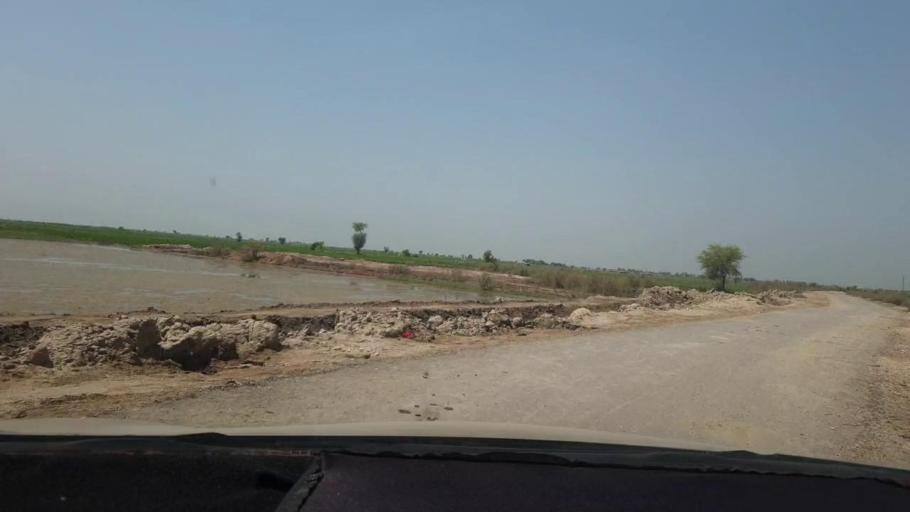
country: PK
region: Sindh
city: Shahdadkot
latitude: 27.8333
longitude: 67.8792
